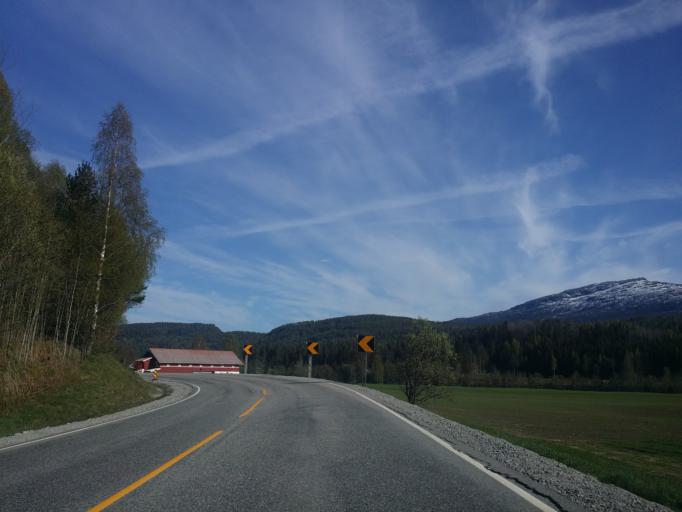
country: NO
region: Telemark
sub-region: Hjartdal
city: Sauland
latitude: 59.6217
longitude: 8.9114
